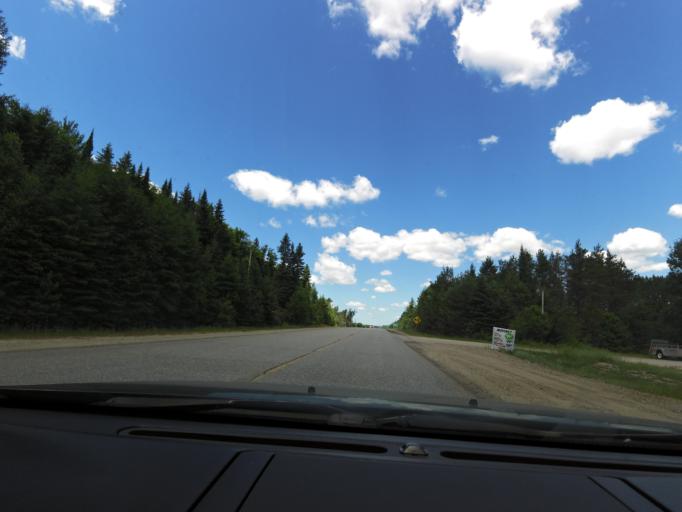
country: CA
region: Ontario
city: Huntsville
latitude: 45.5229
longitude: -79.3161
